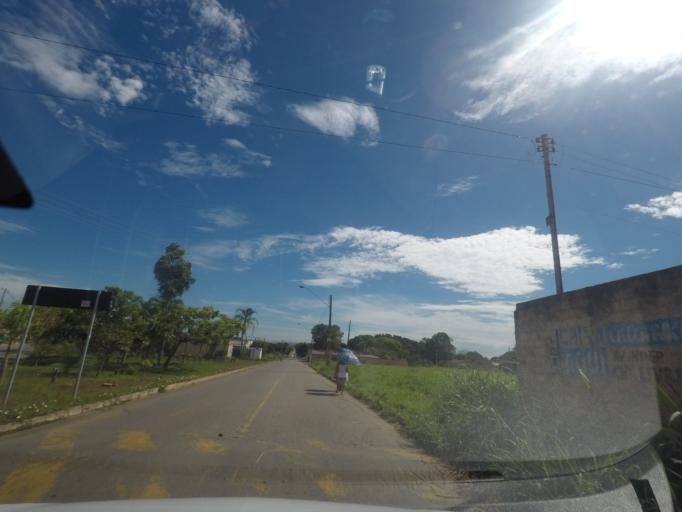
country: BR
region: Goias
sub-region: Aparecida De Goiania
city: Aparecida de Goiania
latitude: -16.8188
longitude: -49.2935
